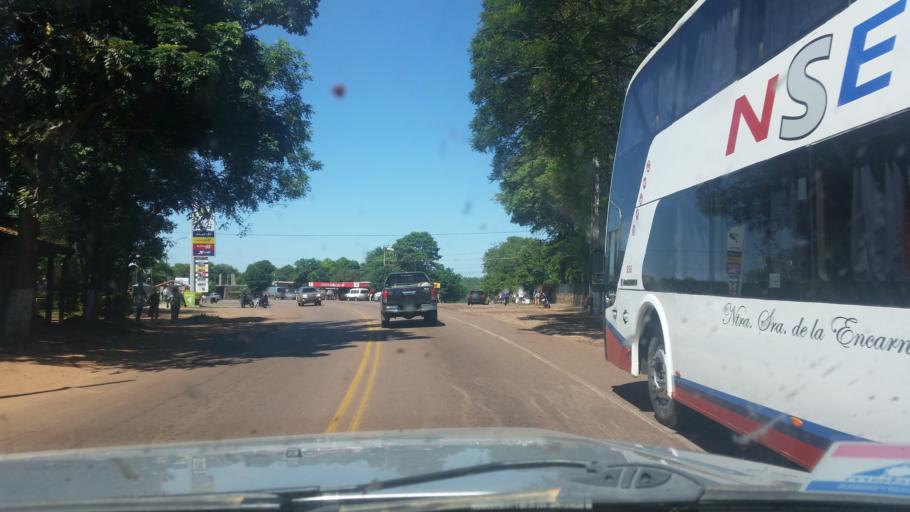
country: PY
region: Paraguari
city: Quiindy
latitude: -25.8812
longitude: -57.2901
